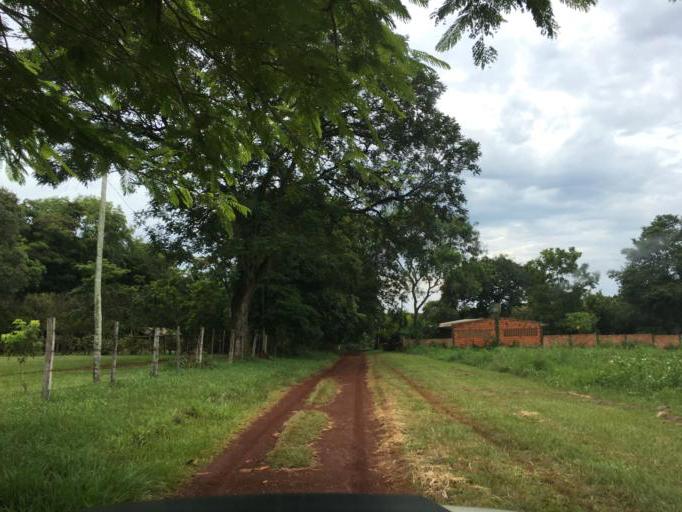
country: PY
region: Alto Parana
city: Ciudad del Este
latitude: -25.4129
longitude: -54.6545
